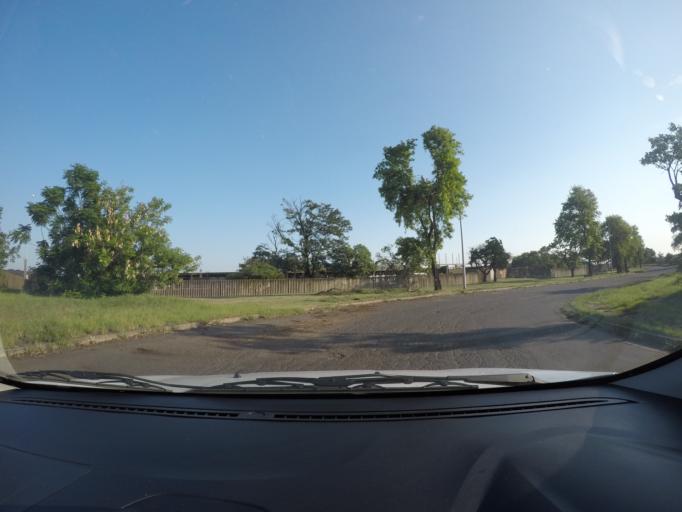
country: ZA
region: KwaZulu-Natal
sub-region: uThungulu District Municipality
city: Richards Bay
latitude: -28.7577
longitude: 32.0102
